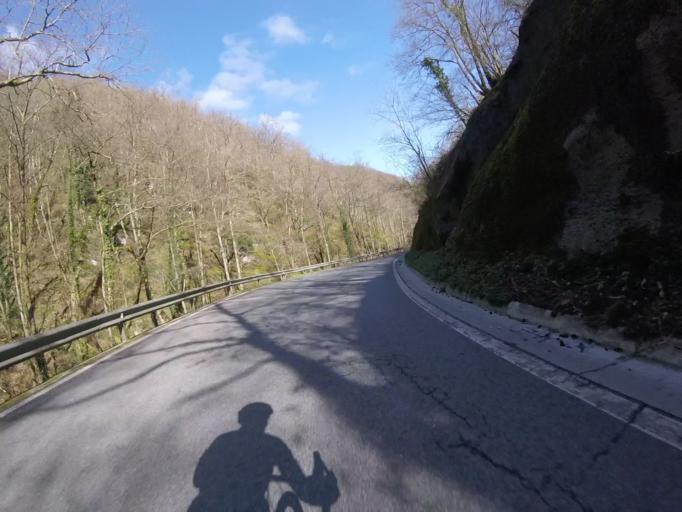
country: ES
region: Navarre
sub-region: Provincia de Navarra
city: Ezkurra
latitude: 43.1141
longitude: -1.8539
